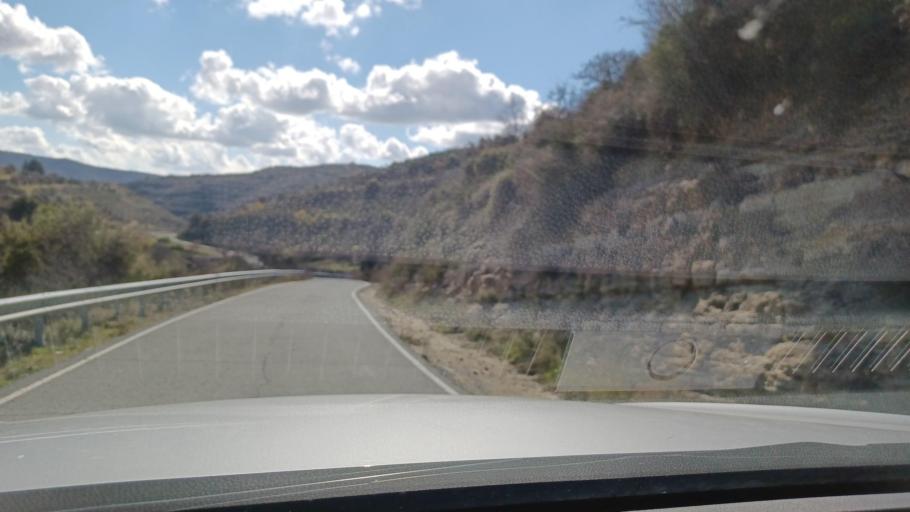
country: CY
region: Limassol
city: Pachna
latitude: 34.8188
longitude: 32.7789
